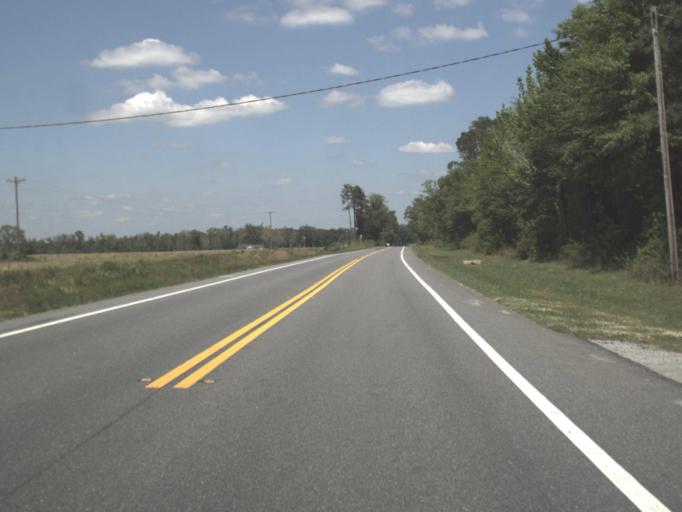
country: US
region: Alabama
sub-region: Escambia County
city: East Brewton
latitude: 30.9723
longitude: -87.0467
